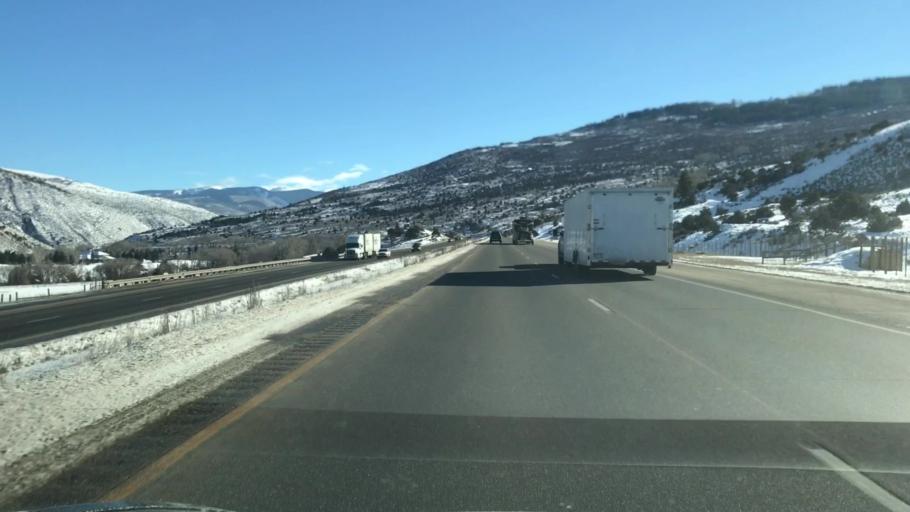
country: US
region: Colorado
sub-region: Eagle County
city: Edwards
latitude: 39.6910
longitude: -106.6628
